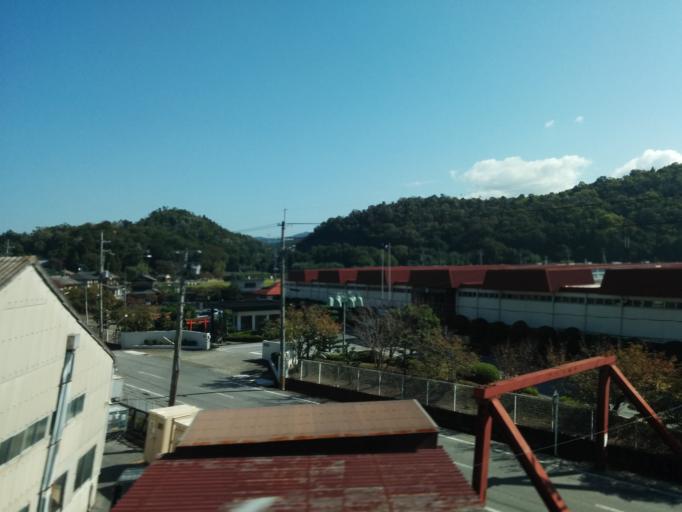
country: JP
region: Shiga Prefecture
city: Nagahama
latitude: 35.3282
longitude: 136.2927
